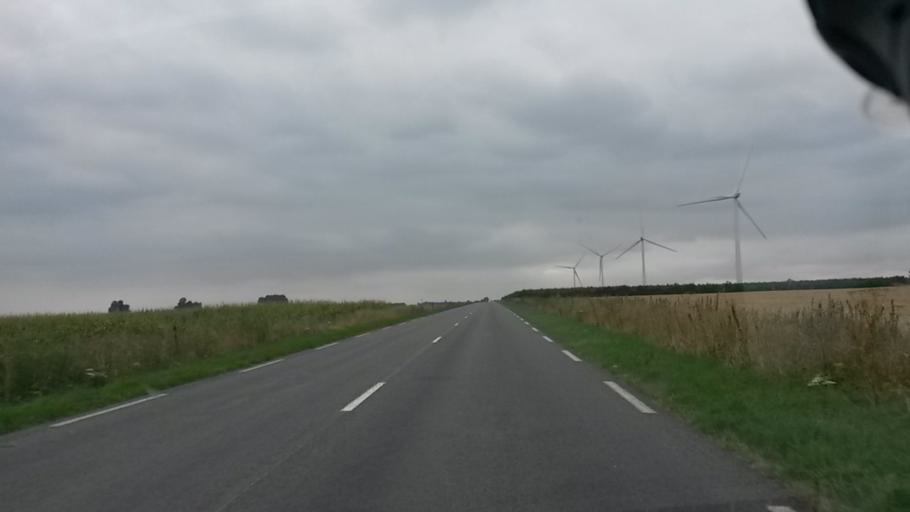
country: FR
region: Haute-Normandie
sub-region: Departement de la Seine-Maritime
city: Aumale
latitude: 49.7715
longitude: 1.8371
